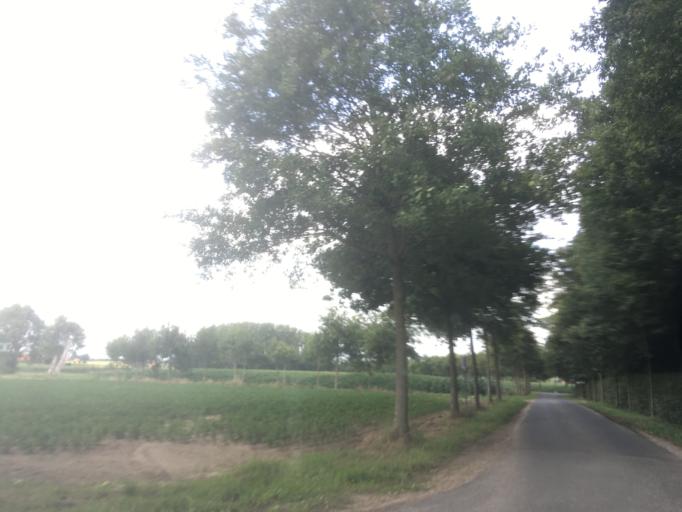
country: BE
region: Flanders
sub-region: Provincie West-Vlaanderen
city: Moorslede
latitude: 50.9061
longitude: 3.0960
